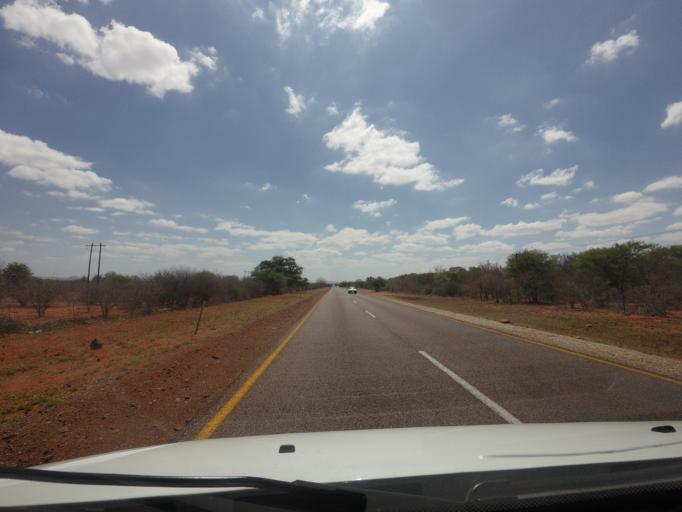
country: ZA
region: Limpopo
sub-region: Capricorn District Municipality
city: Dendron
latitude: -23.5509
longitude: 28.7355
